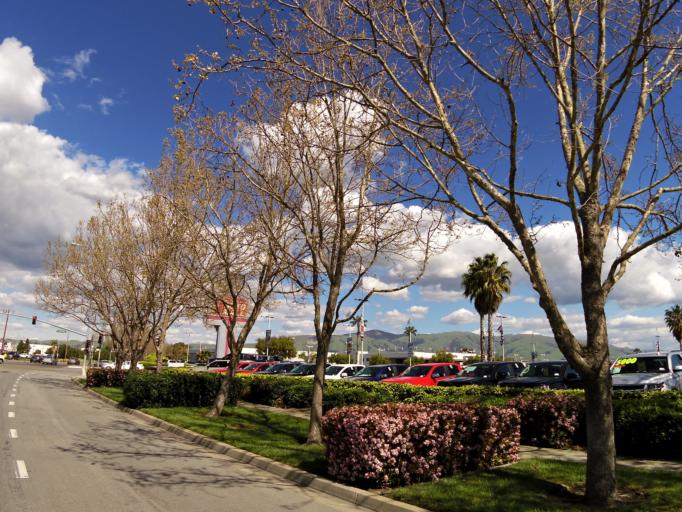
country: US
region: California
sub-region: Alameda County
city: Fremont
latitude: 37.5018
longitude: -121.9799
